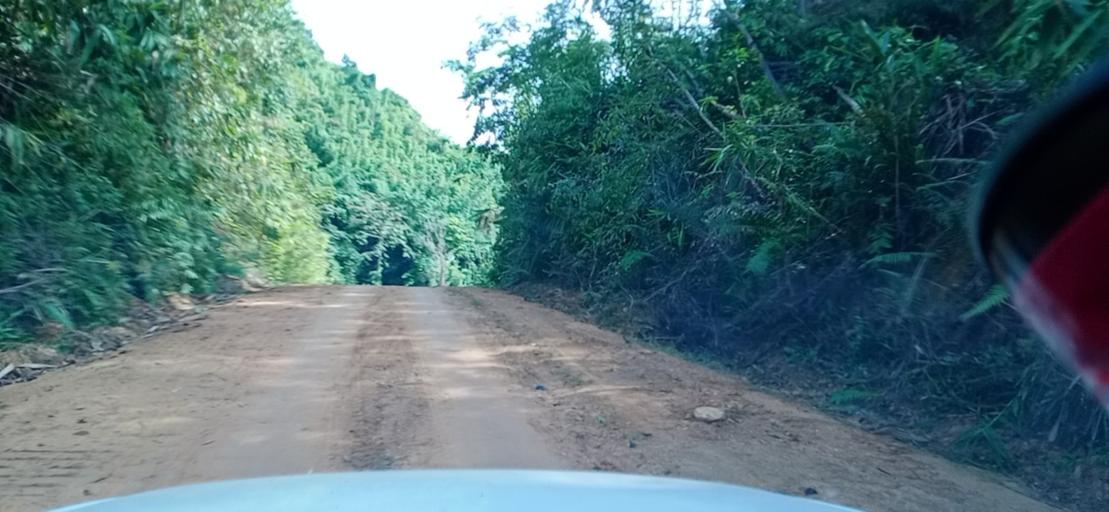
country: TH
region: Changwat Bueng Kan
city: Pak Khat
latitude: 18.6371
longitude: 103.2532
